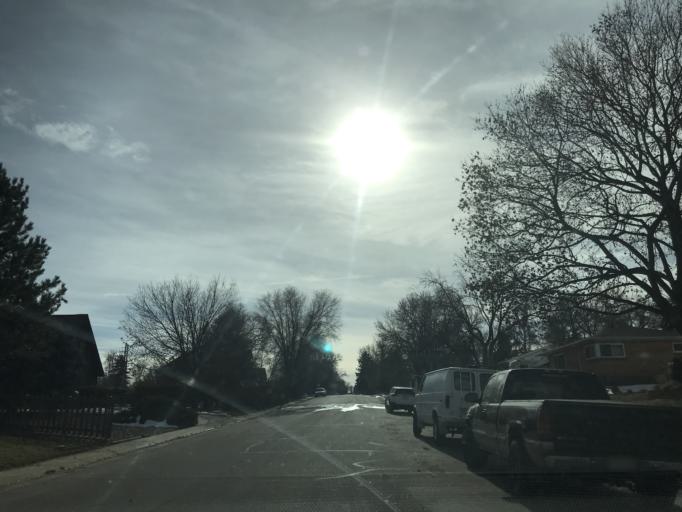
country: US
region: Colorado
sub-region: Arapahoe County
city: Littleton
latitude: 39.6037
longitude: -105.0093
